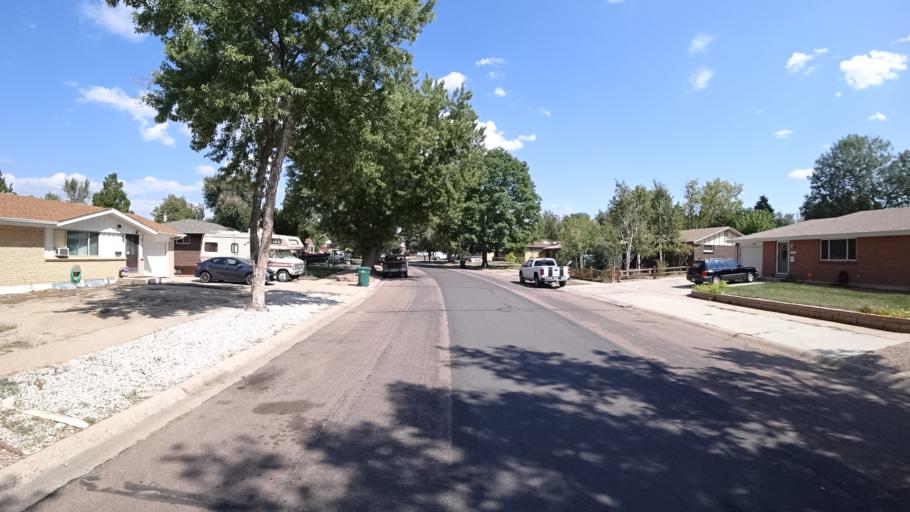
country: US
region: Colorado
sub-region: El Paso County
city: Colorado Springs
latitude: 38.8301
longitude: -104.7682
